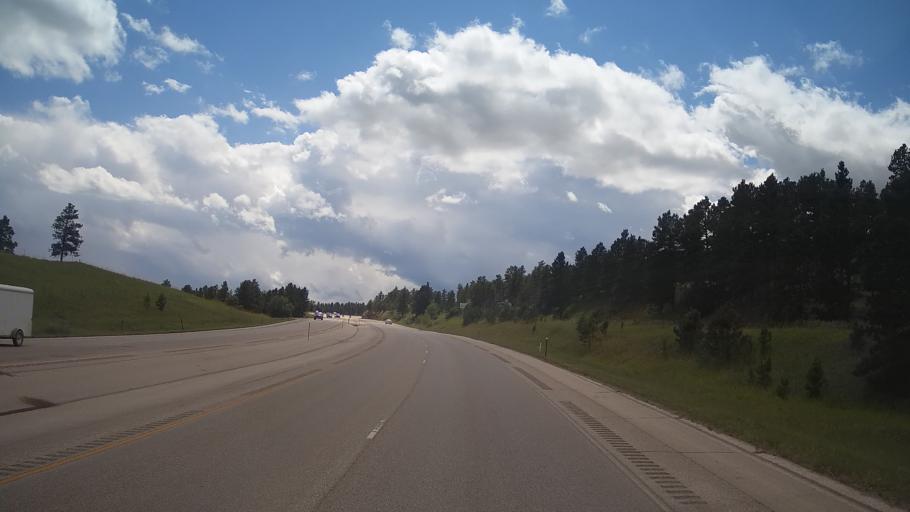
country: US
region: South Dakota
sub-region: Pennington County
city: Colonial Pine Hills
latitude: 43.9810
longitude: -103.2767
